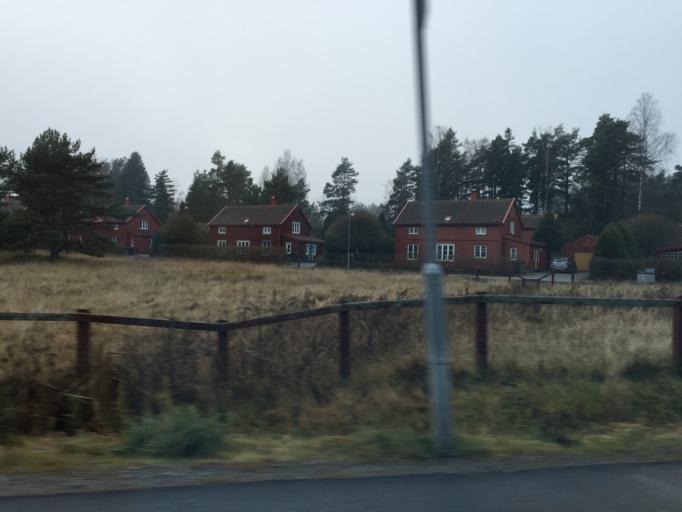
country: SE
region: Stockholm
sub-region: Nynashamns Kommun
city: Osmo
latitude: 59.0268
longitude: 17.9360
